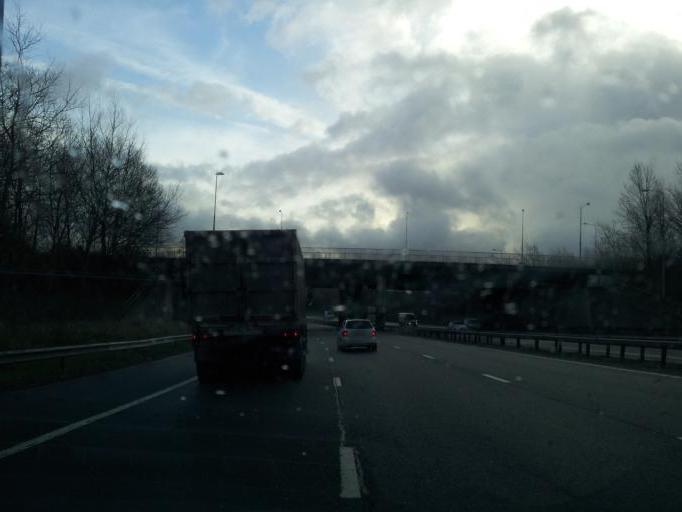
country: GB
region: England
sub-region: Manchester
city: Crumpsall
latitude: 53.5402
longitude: -2.2377
